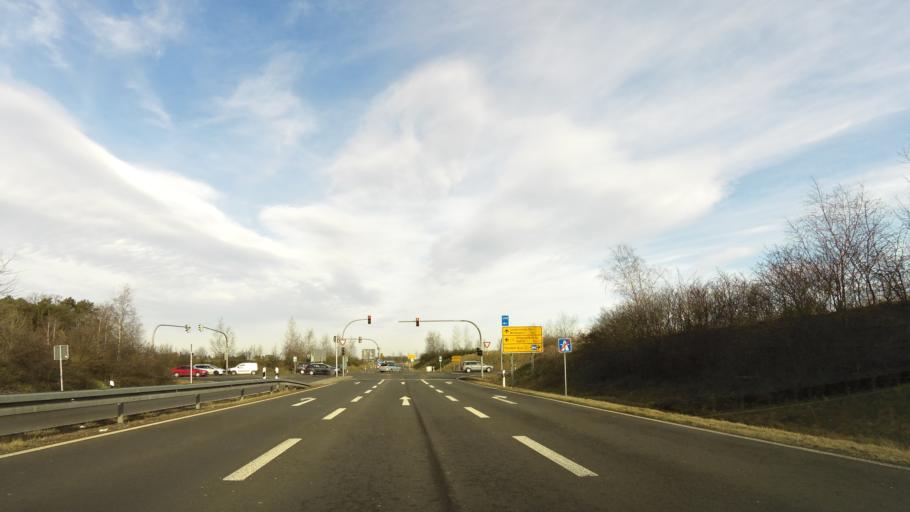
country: DE
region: Brandenburg
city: Michendorf
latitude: 52.3006
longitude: 13.0325
